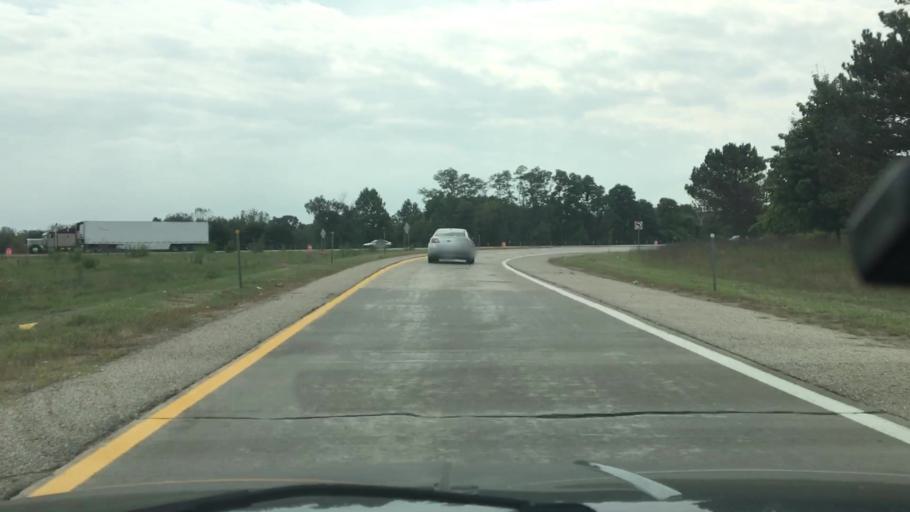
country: US
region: Michigan
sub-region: Berrien County
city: Fair Plain
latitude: 42.0683
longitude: -86.4389
